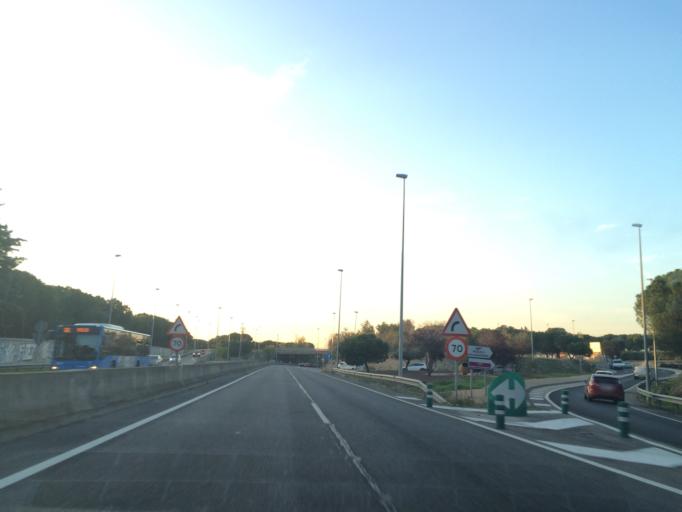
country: ES
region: Madrid
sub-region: Provincia de Madrid
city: Moncloa-Aravaca
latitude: 40.4480
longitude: -3.7597
